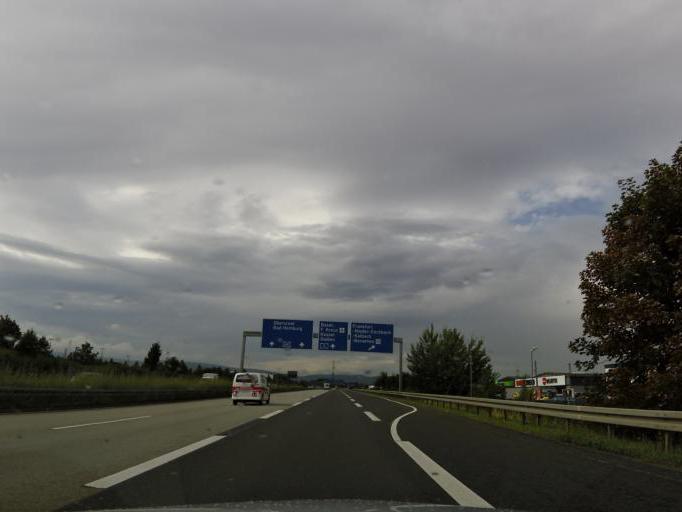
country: DE
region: Hesse
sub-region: Regierungsbezirk Darmstadt
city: Bad Homburg vor der Hoehe
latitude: 50.1927
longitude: 8.6544
